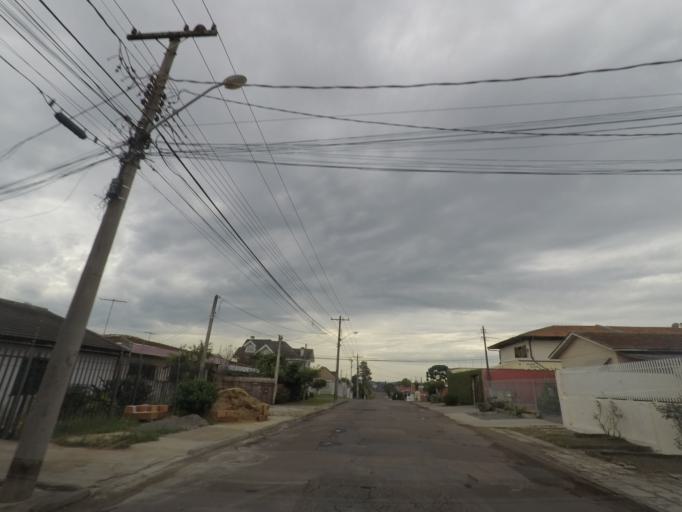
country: BR
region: Parana
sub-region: Curitiba
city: Curitiba
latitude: -25.4723
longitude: -49.3045
